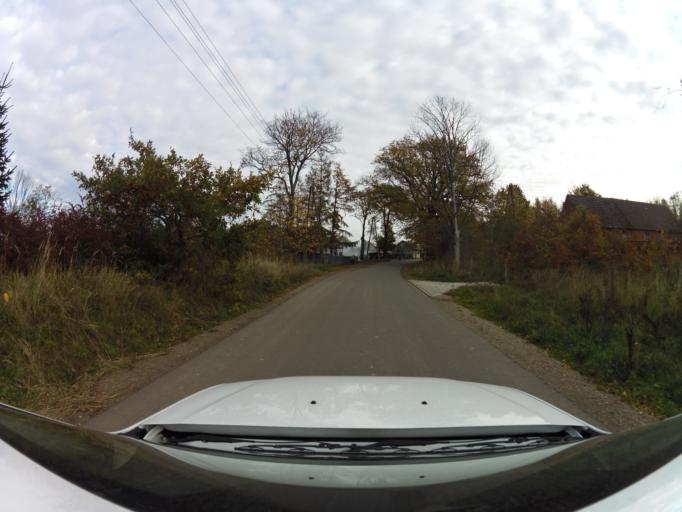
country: PL
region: West Pomeranian Voivodeship
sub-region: Powiat gryficki
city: Cerkwica
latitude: 54.0495
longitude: 15.1054
